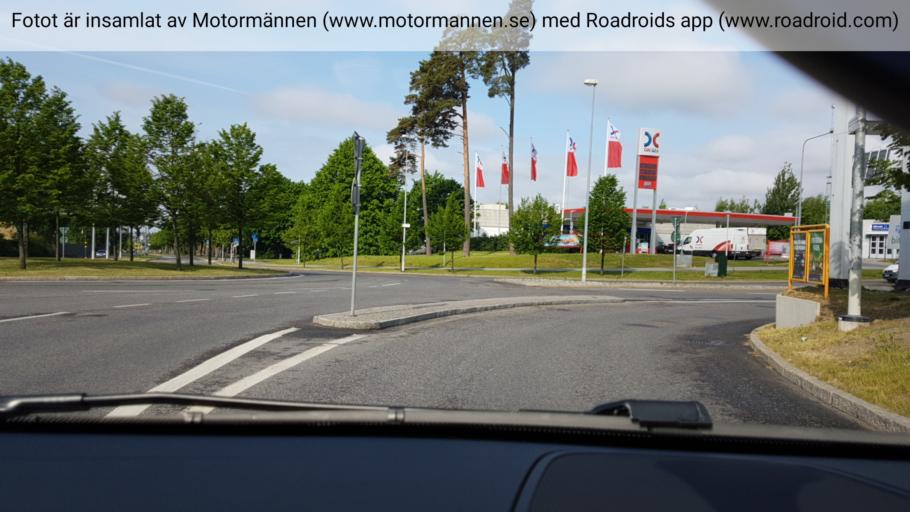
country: SE
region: Stockholm
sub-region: Stockholms Kommun
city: Arsta
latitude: 59.2884
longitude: 18.0867
